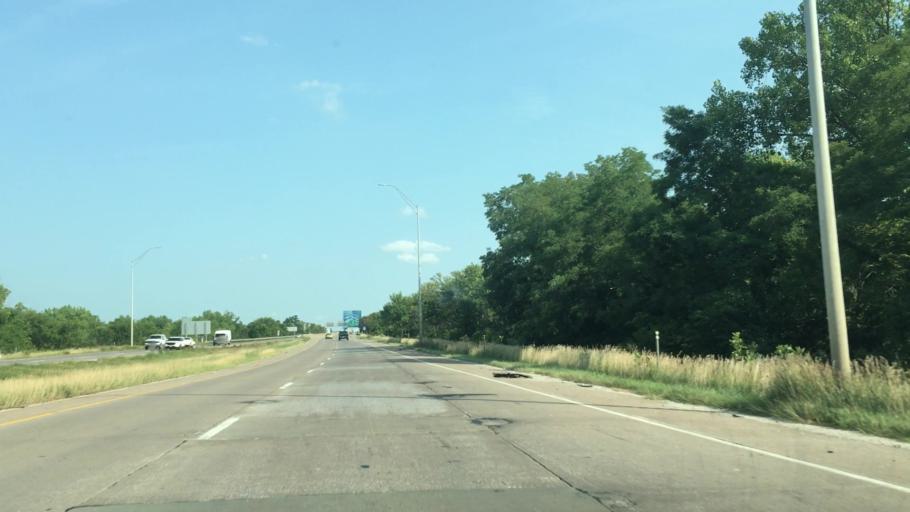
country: US
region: Illinois
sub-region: Rock Island County
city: Rock Island
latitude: 41.4881
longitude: -90.6444
